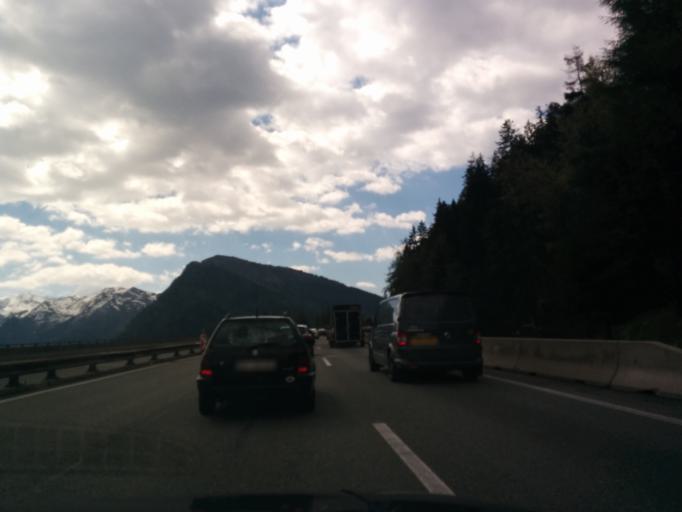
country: AT
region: Tyrol
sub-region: Politischer Bezirk Innsbruck Land
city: Steinach am Brenner
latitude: 47.0729
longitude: 11.4797
